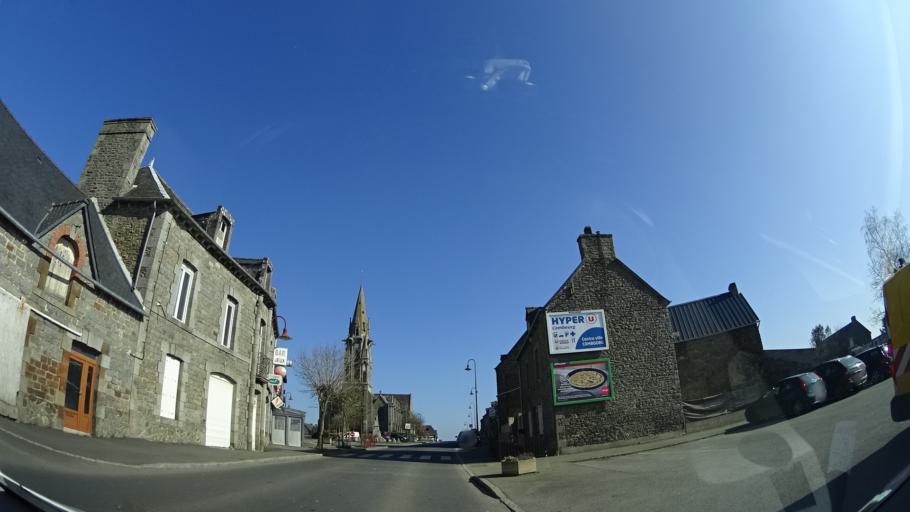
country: FR
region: Brittany
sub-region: Departement d'Ille-et-Vilaine
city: Meillac
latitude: 48.4120
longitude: -1.8140
